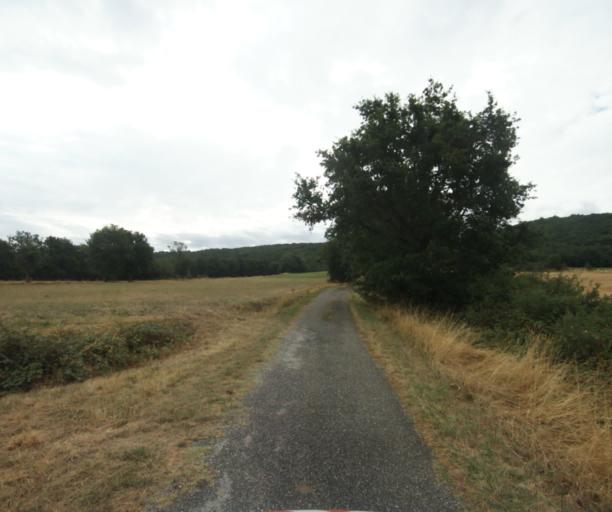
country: FR
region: Midi-Pyrenees
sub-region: Departement de la Haute-Garonne
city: Revel
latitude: 43.4167
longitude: 1.9803
